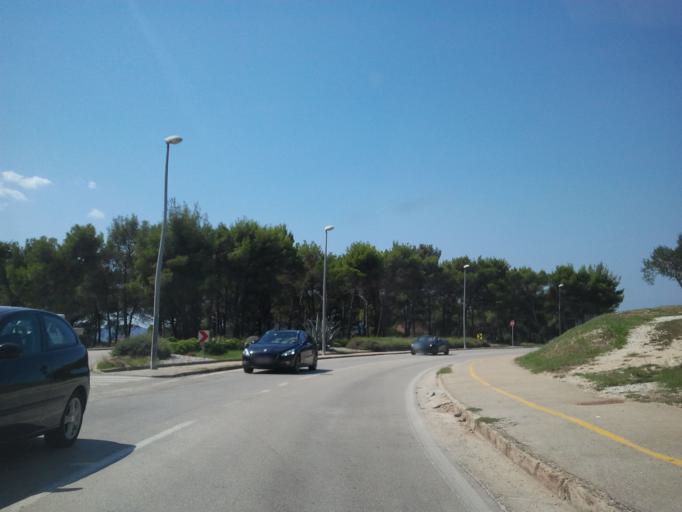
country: HR
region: Zadarska
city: Zadar
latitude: 44.1384
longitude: 15.2269
